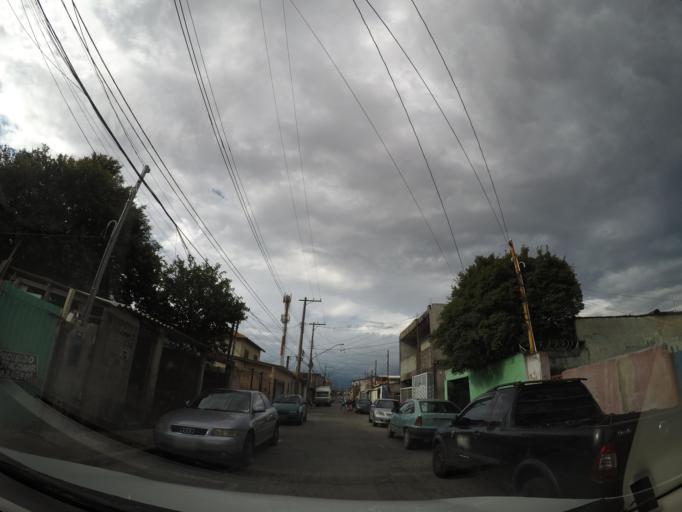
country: BR
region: Sao Paulo
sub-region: Guarulhos
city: Guarulhos
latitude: -23.4802
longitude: -46.5572
